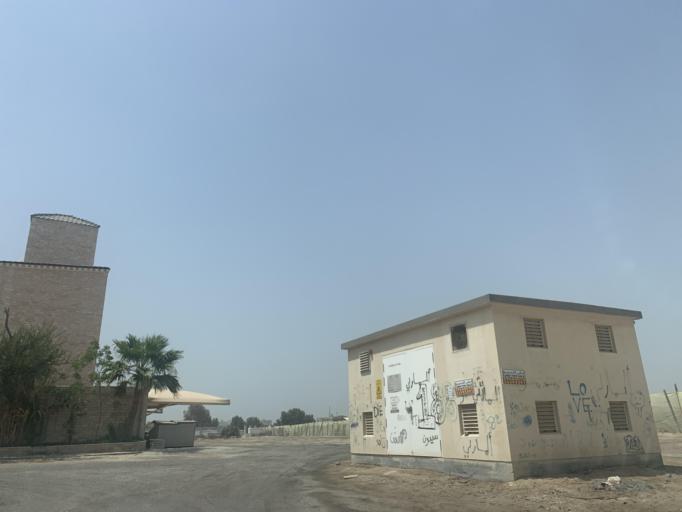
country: BH
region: Manama
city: Jidd Hafs
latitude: 26.2009
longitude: 50.5043
